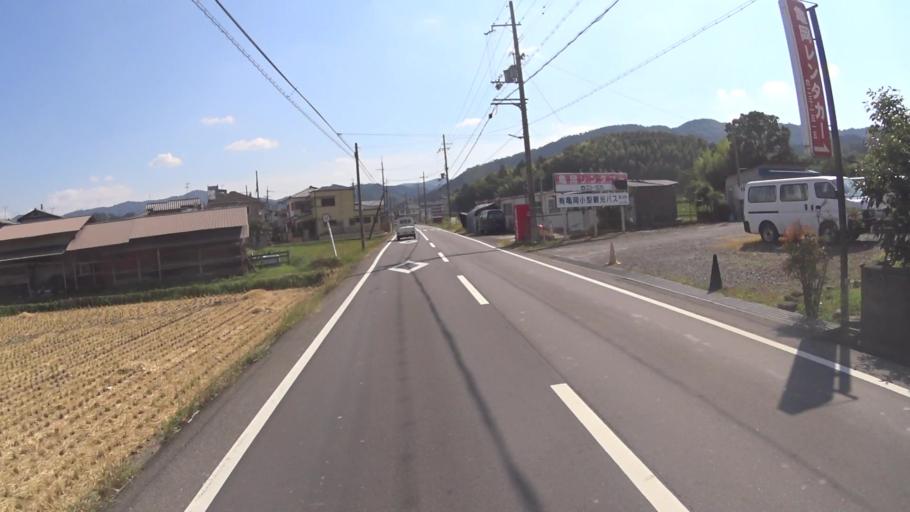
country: JP
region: Kyoto
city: Kameoka
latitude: 35.0073
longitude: 135.5774
